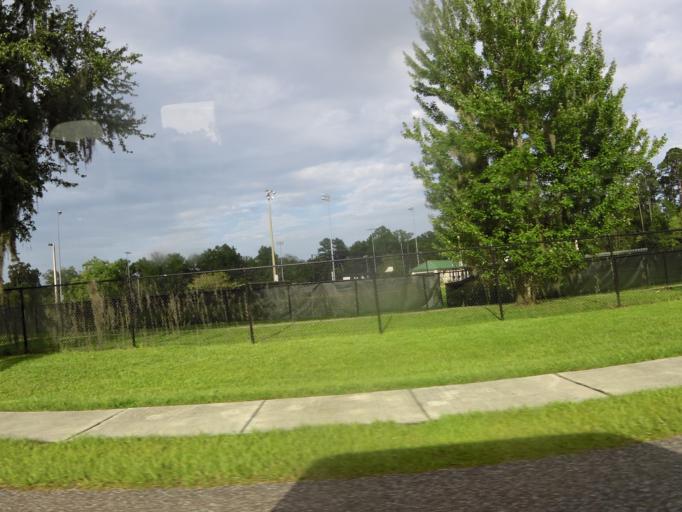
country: US
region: Florida
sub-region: Nassau County
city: Nassau Village-Ratliff
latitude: 30.4240
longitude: -81.7697
